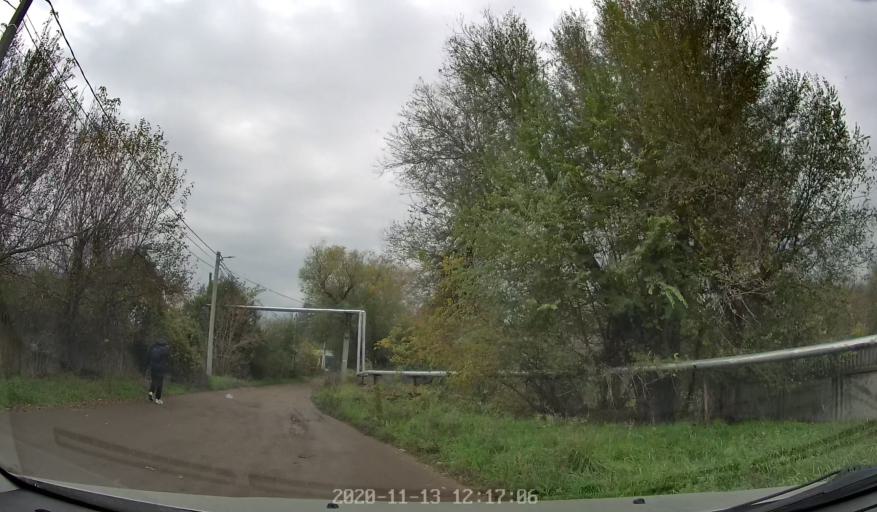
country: MD
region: Laloveni
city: Ialoveni
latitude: 46.9485
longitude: 28.8369
